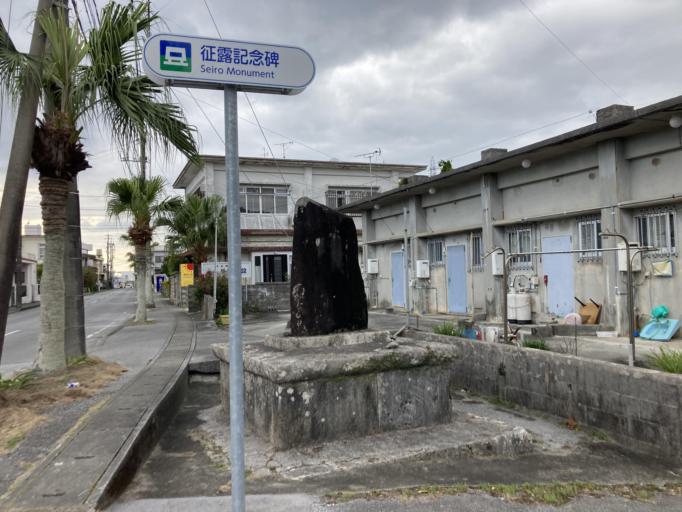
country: JP
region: Okinawa
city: Ishikawa
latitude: 26.4549
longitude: 127.9213
